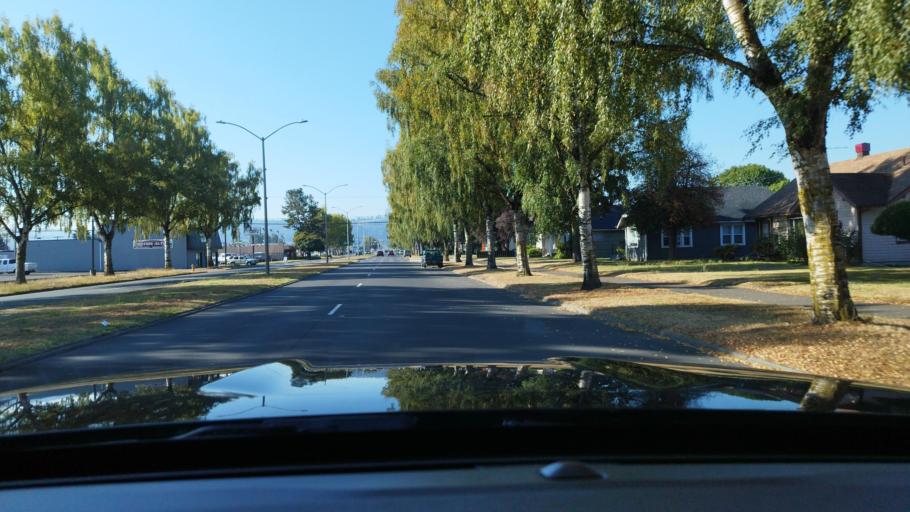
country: US
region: Washington
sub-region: Cowlitz County
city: Longview
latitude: 46.1256
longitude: -122.9423
